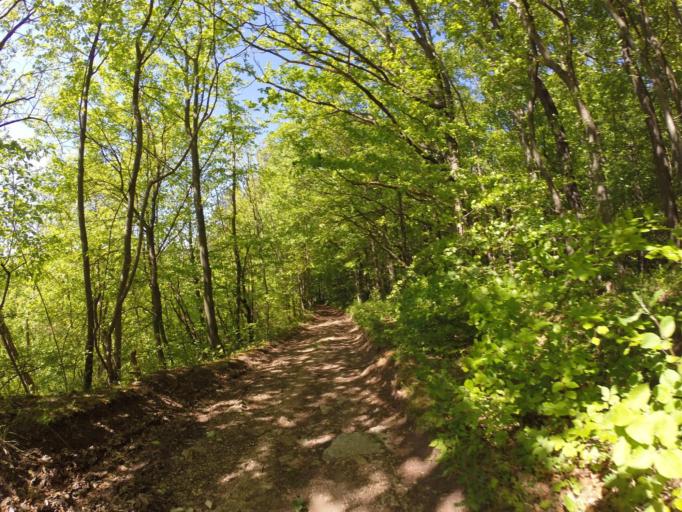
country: DE
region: Thuringia
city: Grosslobichau
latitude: 50.9249
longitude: 11.6650
